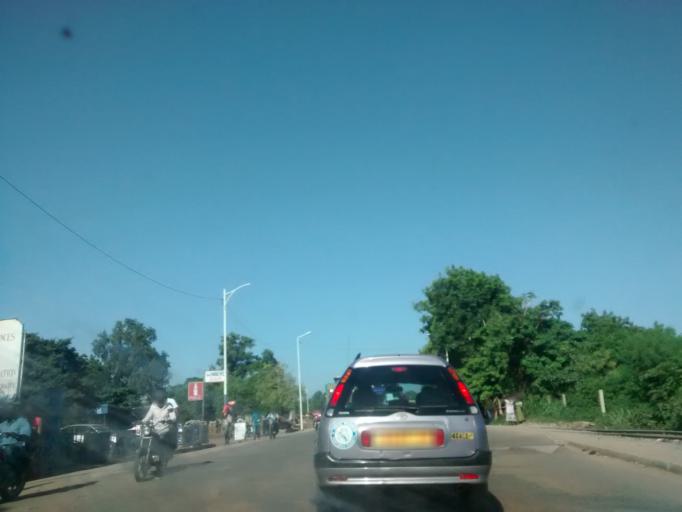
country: TG
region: Maritime
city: Lome
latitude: 6.1697
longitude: 1.1979
